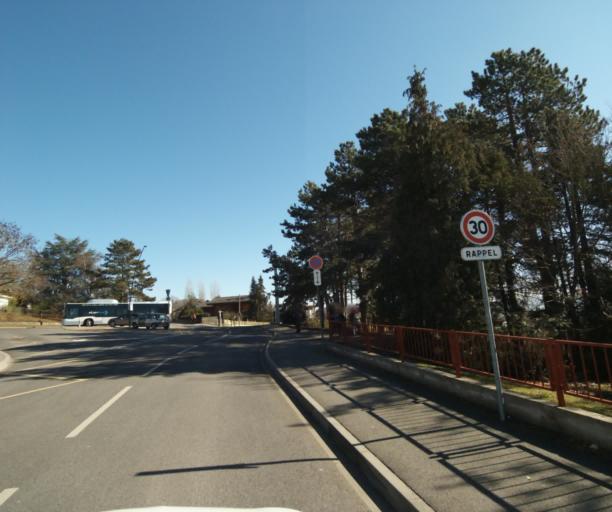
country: FR
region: Lorraine
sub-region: Departement de Meurthe-et-Moselle
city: Saint-Max
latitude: 48.7111
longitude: 6.2091
